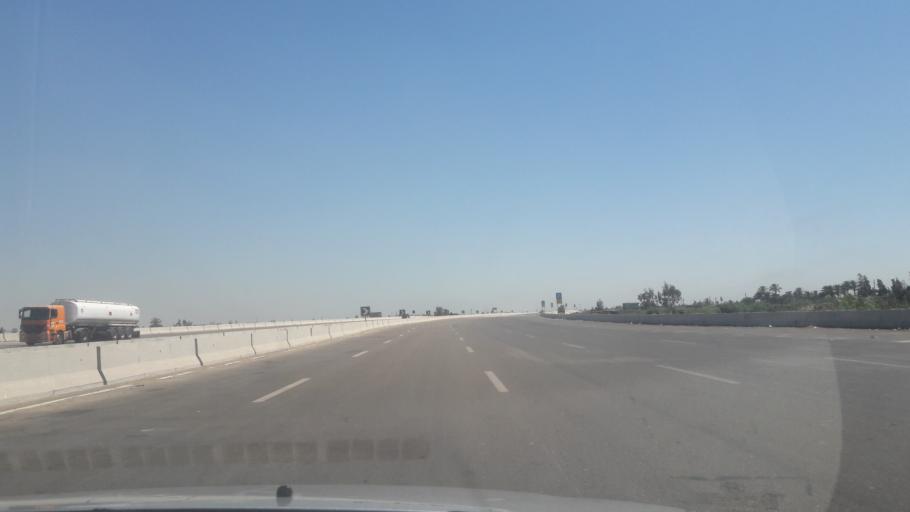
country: EG
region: Muhafazat Bur Sa`id
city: Port Said
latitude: 31.1099
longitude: 32.2339
